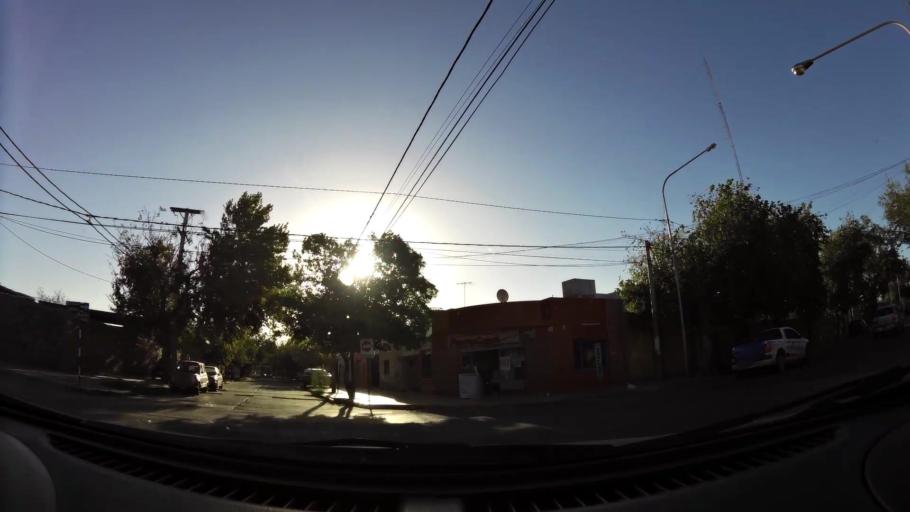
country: AR
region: San Juan
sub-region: Departamento de Santa Lucia
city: Santa Lucia
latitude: -31.5454
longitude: -68.5139
